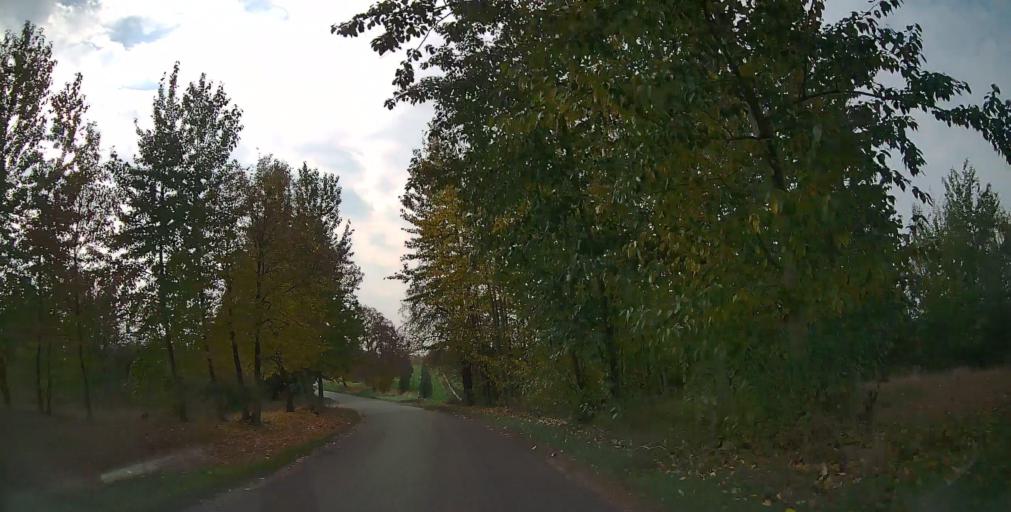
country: PL
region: Masovian Voivodeship
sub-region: Powiat grojecki
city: Mogielnica
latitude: 51.6817
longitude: 20.7143
